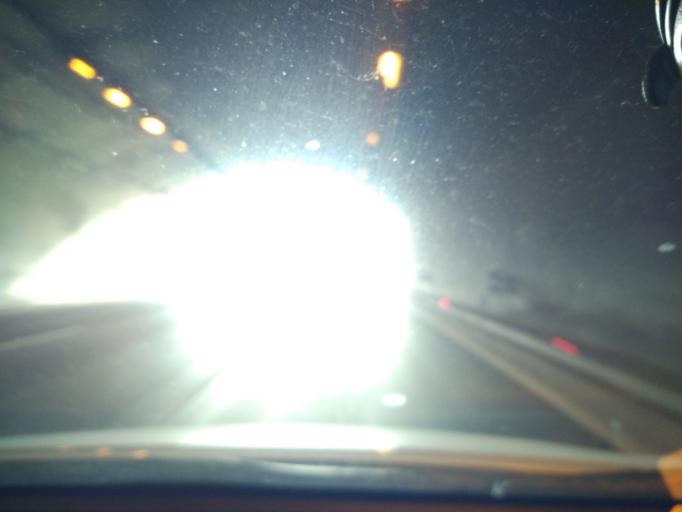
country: TR
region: Kocaeli
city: Tavsancil
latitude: 40.7739
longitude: 29.5503
